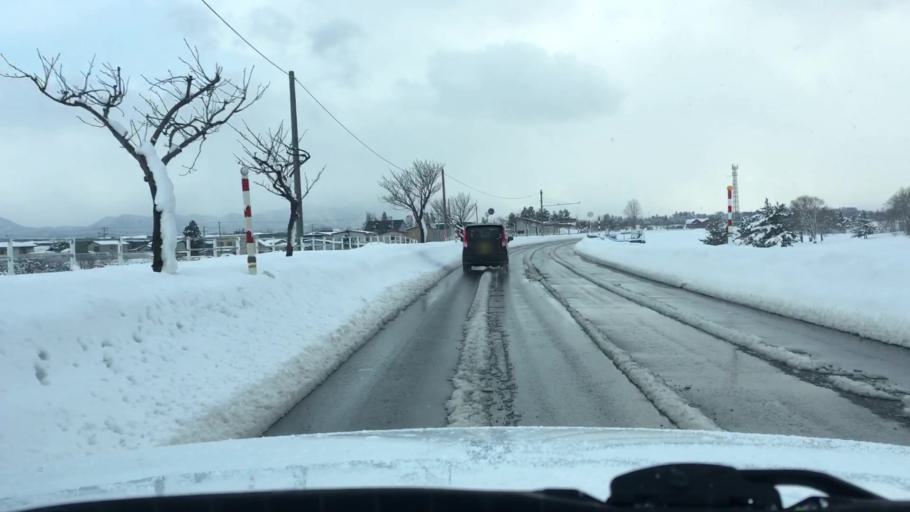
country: JP
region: Aomori
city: Hirosaki
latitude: 40.6261
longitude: 140.4740
